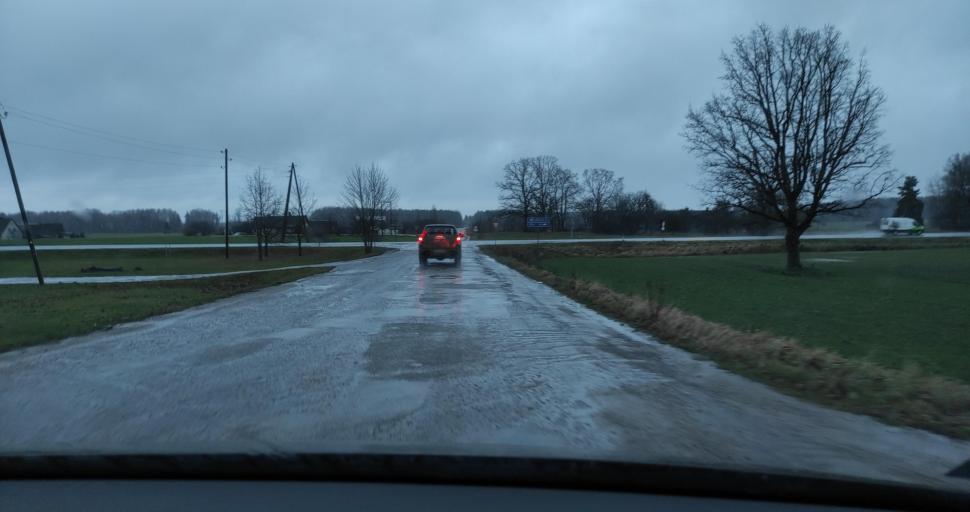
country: LV
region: Skrunda
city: Skrunda
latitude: 56.6763
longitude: 22.2199
